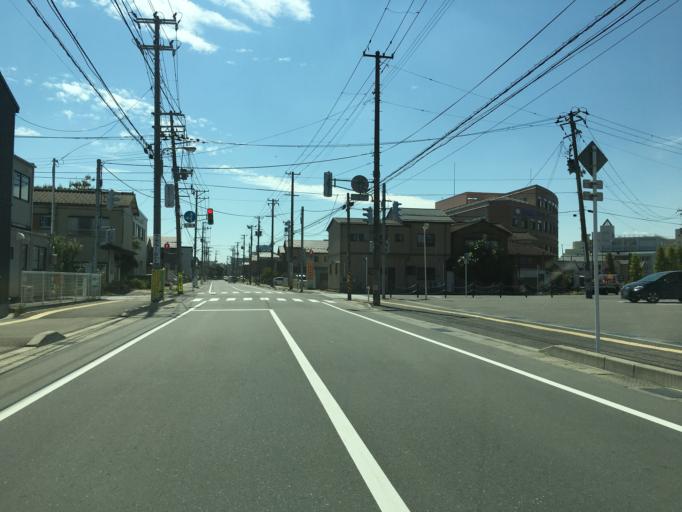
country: JP
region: Niigata
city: Niigata-shi
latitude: 37.9353
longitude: 139.0570
